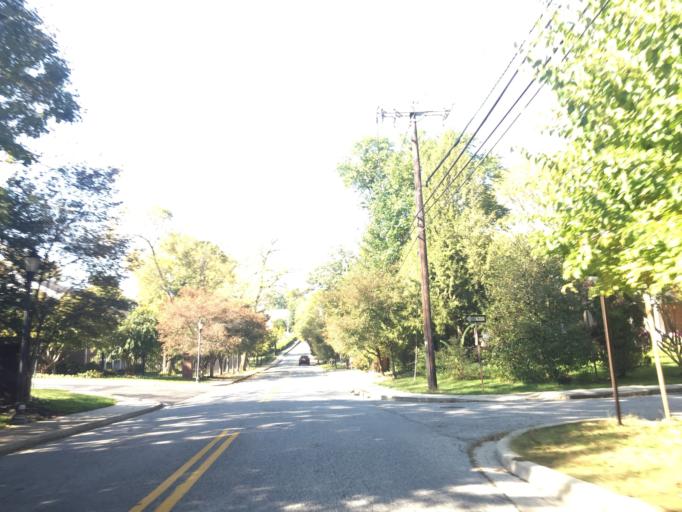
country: US
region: Maryland
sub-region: Baltimore County
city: Towson
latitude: 39.3539
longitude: -76.6146
